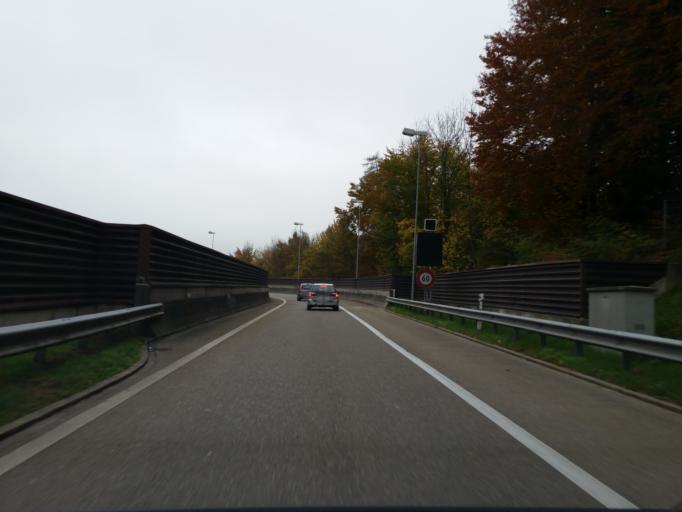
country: CH
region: Saint Gallen
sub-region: Wahlkreis St. Gallen
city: Sankt Gallen
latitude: 47.4296
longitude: 9.3625
